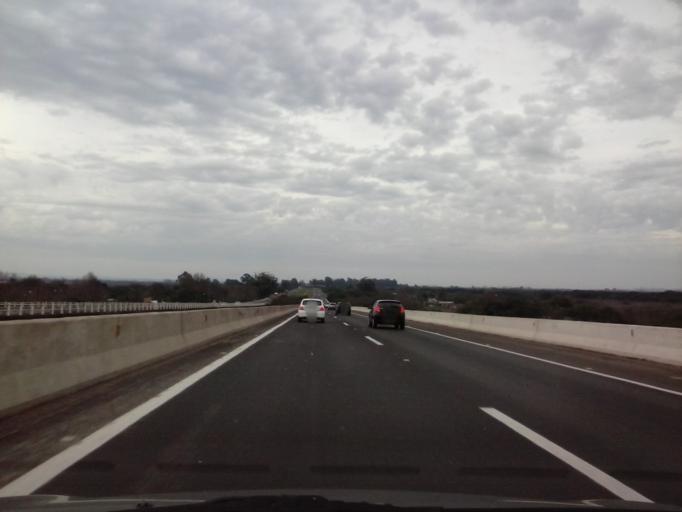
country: BR
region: Rio Grande do Sul
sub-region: Porto Alegre
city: Porto Alegre
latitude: -29.9906
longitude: -51.2671
